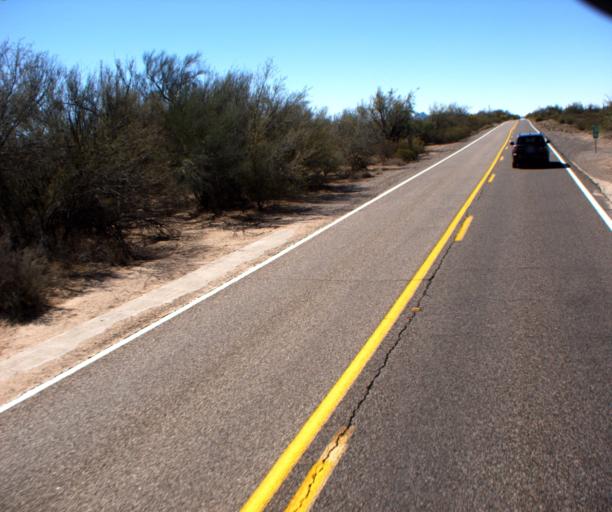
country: US
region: Arizona
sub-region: Pima County
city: Ajo
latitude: 32.1831
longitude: -112.7615
